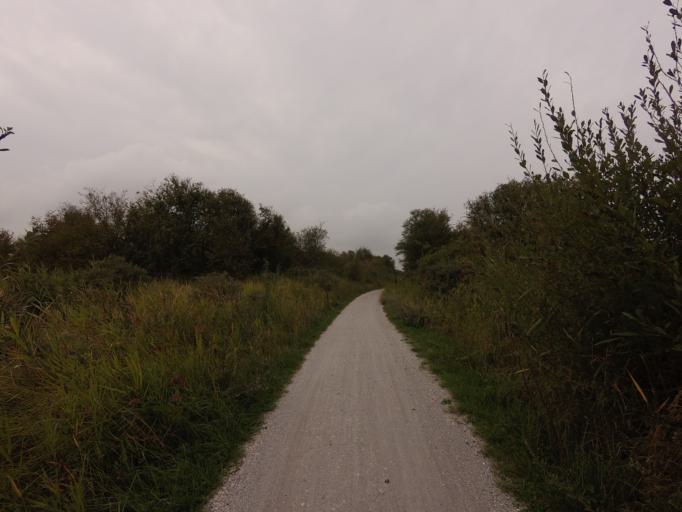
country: NL
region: Friesland
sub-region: Gemeente Schiermonnikoog
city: Schiermonnikoog
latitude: 53.4904
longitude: 6.2010
